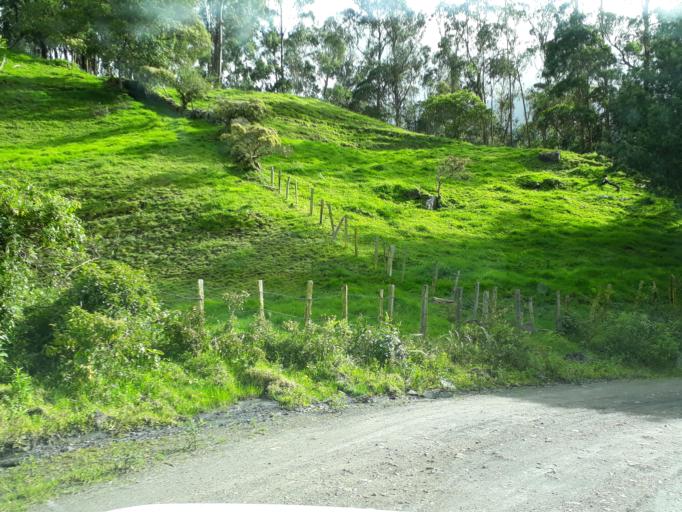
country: CO
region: Cundinamarca
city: Junin
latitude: 4.7843
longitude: -73.6861
